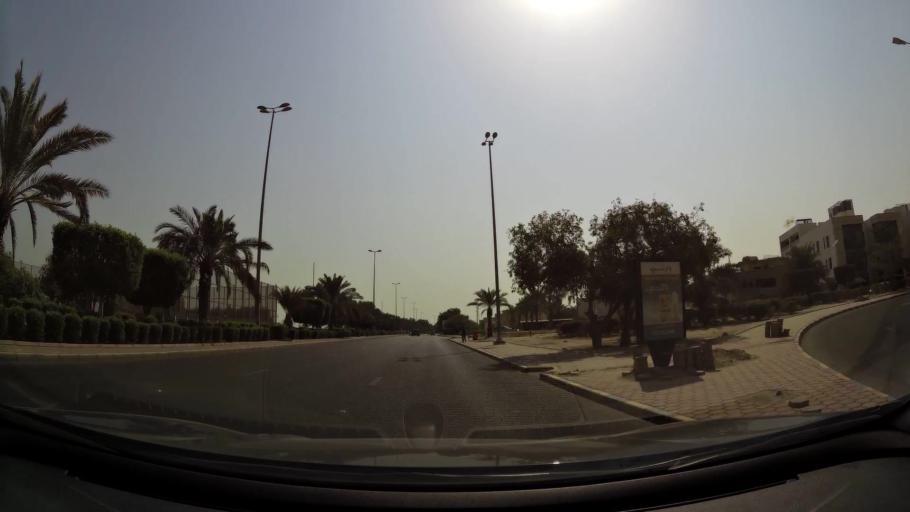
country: KW
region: Al Ahmadi
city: Al Fintas
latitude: 29.1799
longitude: 48.1201
